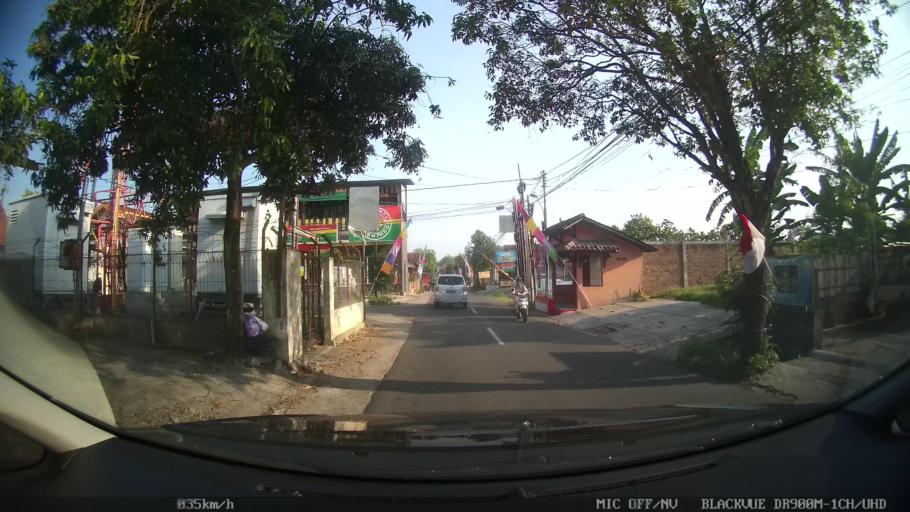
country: ID
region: Daerah Istimewa Yogyakarta
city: Depok
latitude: -7.7757
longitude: 110.4046
